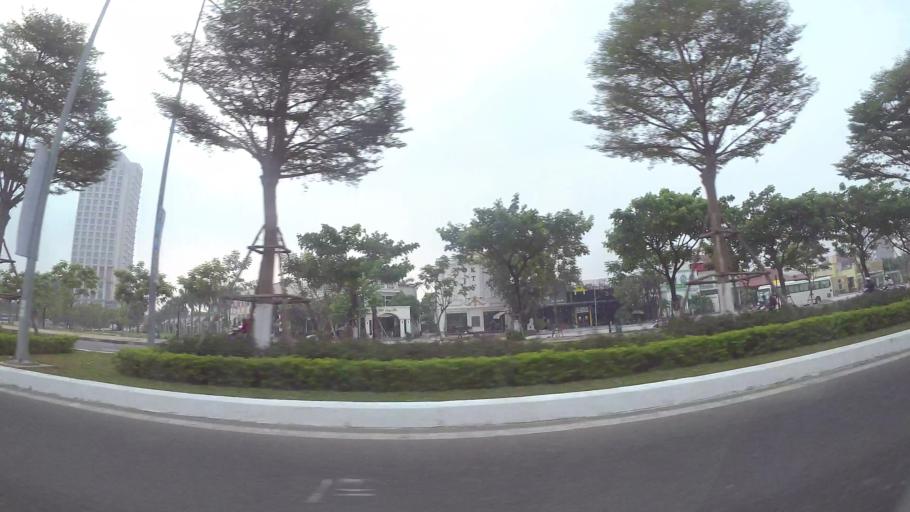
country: VN
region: Da Nang
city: Son Tra
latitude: 16.0497
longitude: 108.2247
